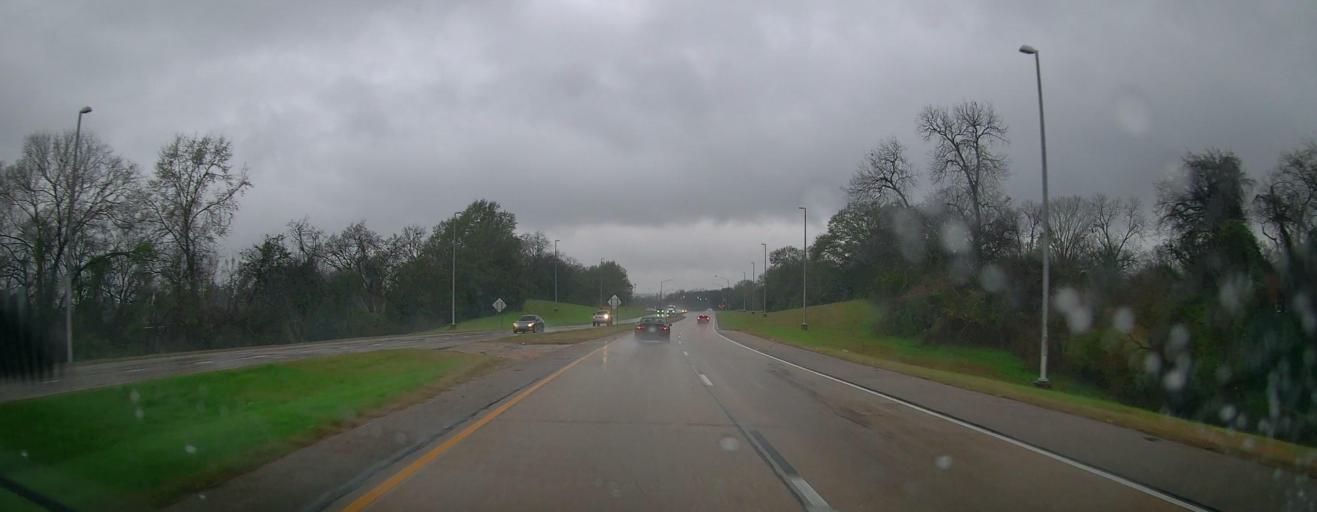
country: US
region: Alabama
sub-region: Montgomery County
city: Montgomery
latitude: 32.3676
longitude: -86.3259
